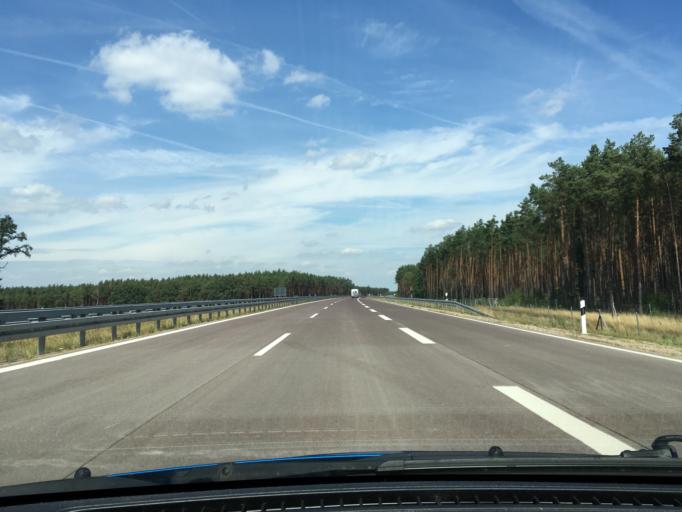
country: DE
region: Mecklenburg-Vorpommern
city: Ludwigslust
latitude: 53.3467
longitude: 11.5184
